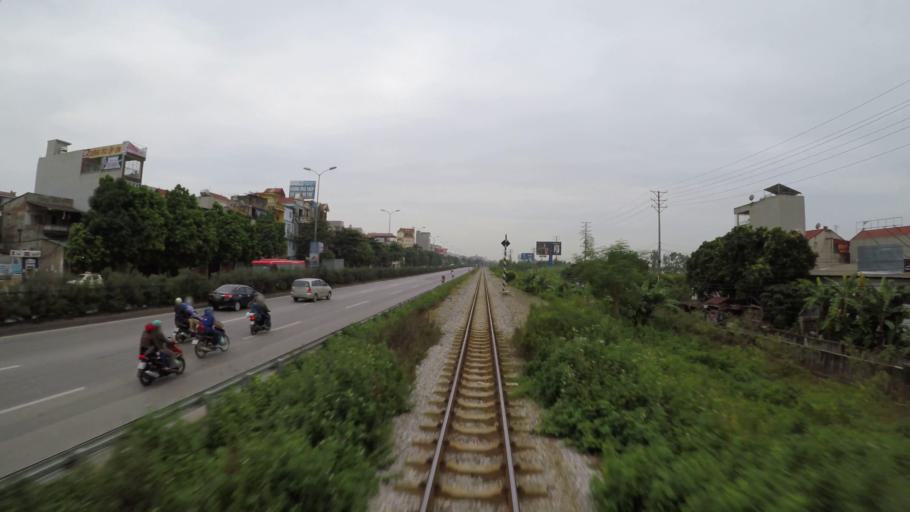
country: VN
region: Hung Yen
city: Nhu Quynh
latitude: 20.9881
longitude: 105.9764
